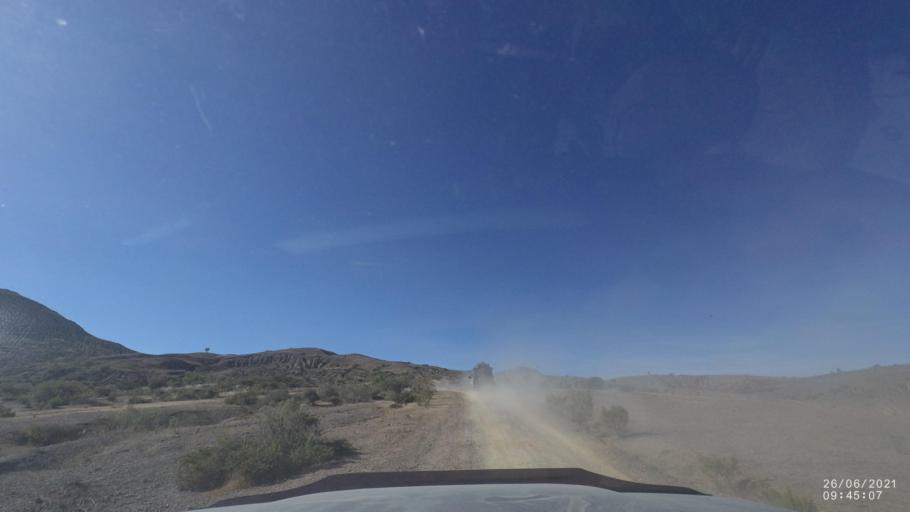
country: BO
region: Cochabamba
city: Mizque
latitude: -17.9471
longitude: -65.6314
